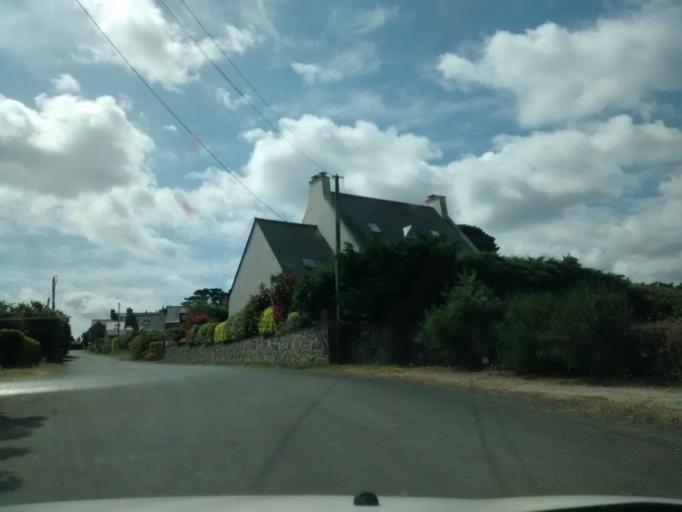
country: FR
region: Brittany
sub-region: Departement des Cotes-d'Armor
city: Penvenan
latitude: 48.8358
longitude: -3.2847
